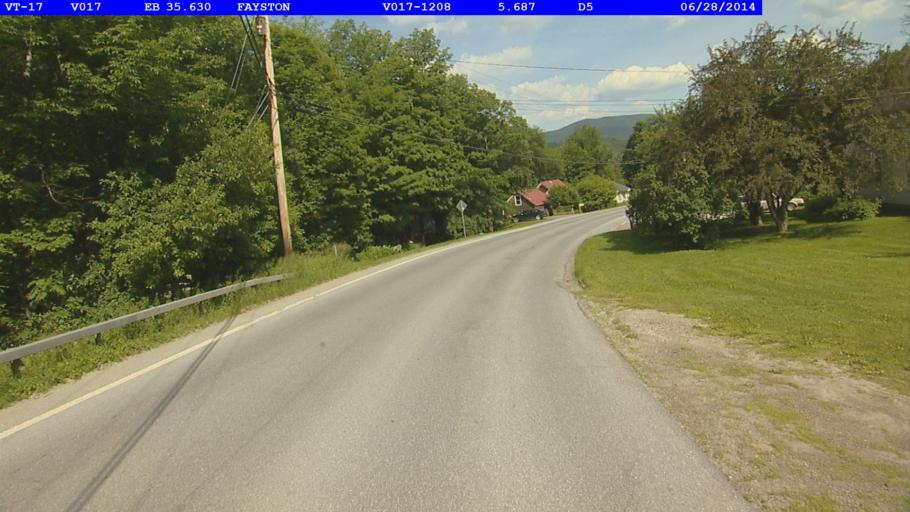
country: US
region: Vermont
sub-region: Washington County
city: Waterbury
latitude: 44.1823
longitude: -72.8457
